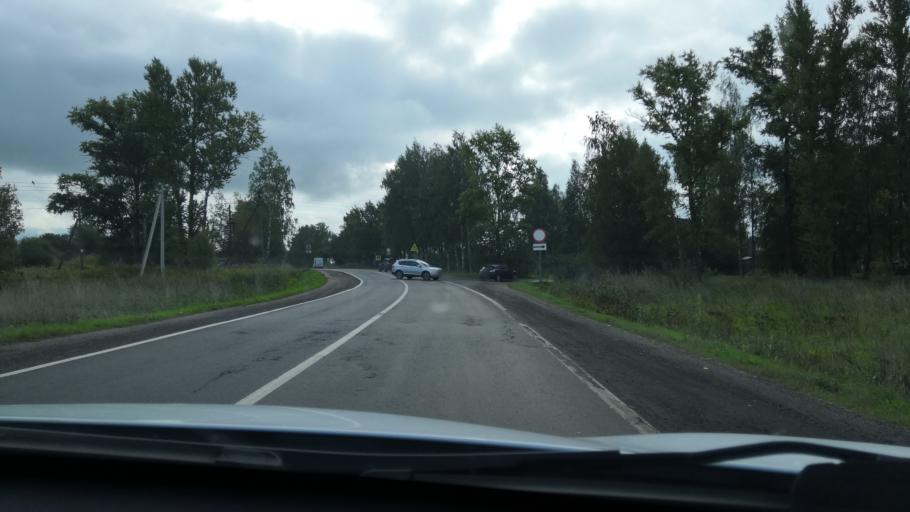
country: RU
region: St.-Petersburg
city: Tyarlevo
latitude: 59.7111
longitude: 30.4691
